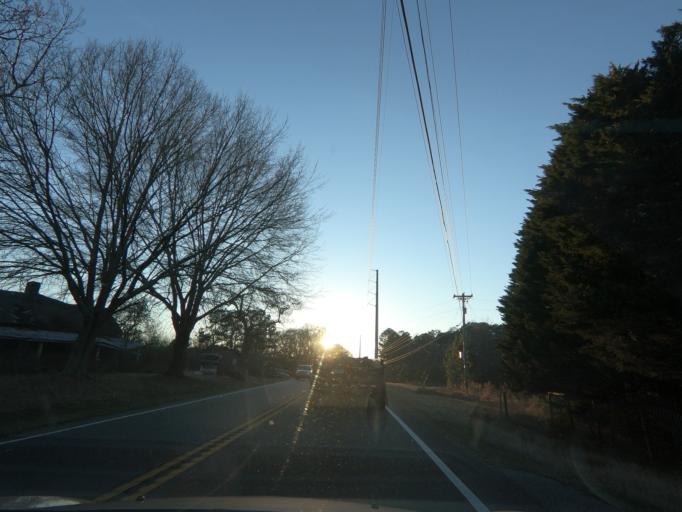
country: US
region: Georgia
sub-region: Forsyth County
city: Cumming
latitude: 34.2993
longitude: -84.1731
